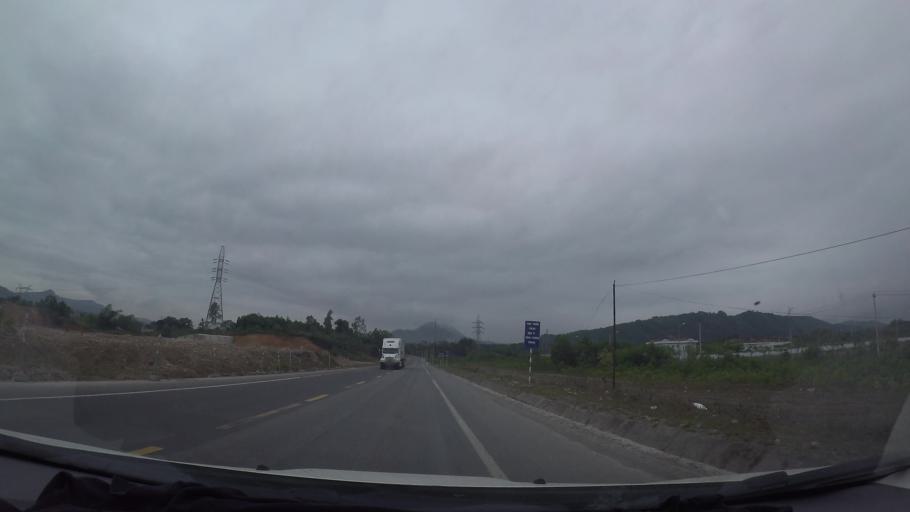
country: VN
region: Da Nang
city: Lien Chieu
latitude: 16.0840
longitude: 108.0847
